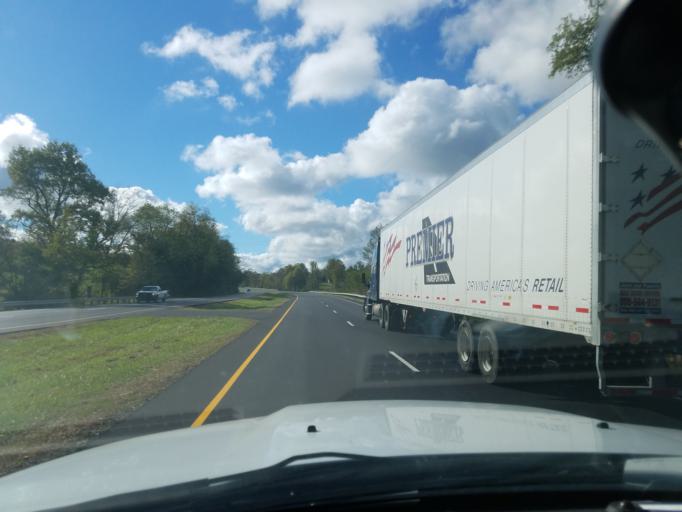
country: US
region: Kentucky
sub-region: Boyle County
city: Danville
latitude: 37.6023
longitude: -84.7280
